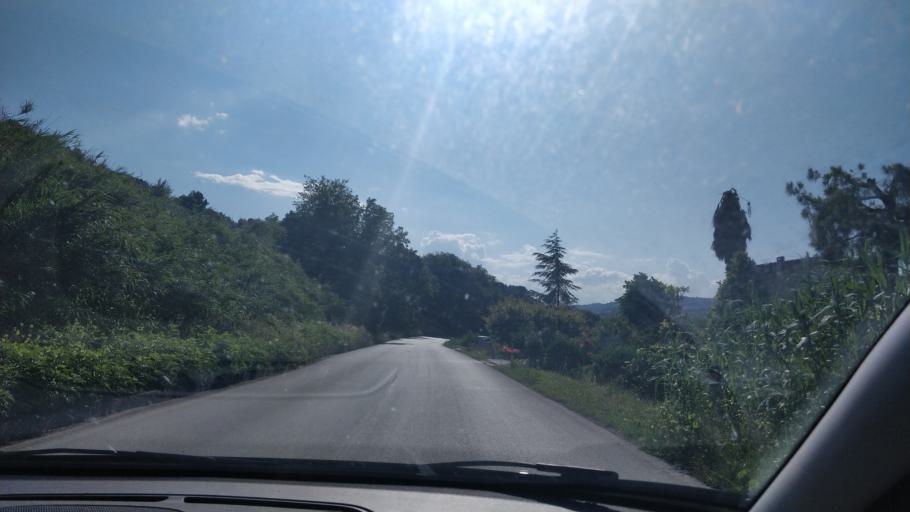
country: IT
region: The Marches
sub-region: Provincia di Ascoli Piceno
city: Cupra Marittima
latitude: 43.0347
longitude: 13.8478
